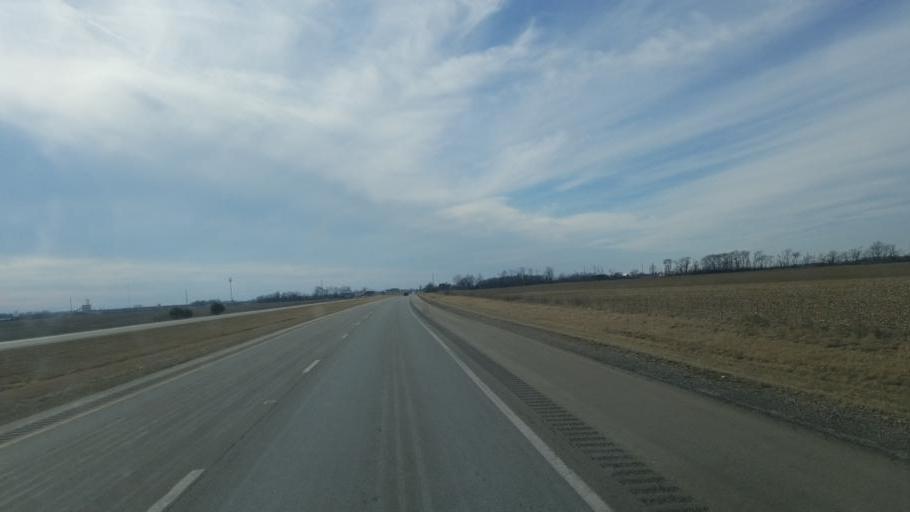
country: US
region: Ohio
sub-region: Van Wert County
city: Van Wert
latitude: 40.8871
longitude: -84.5938
